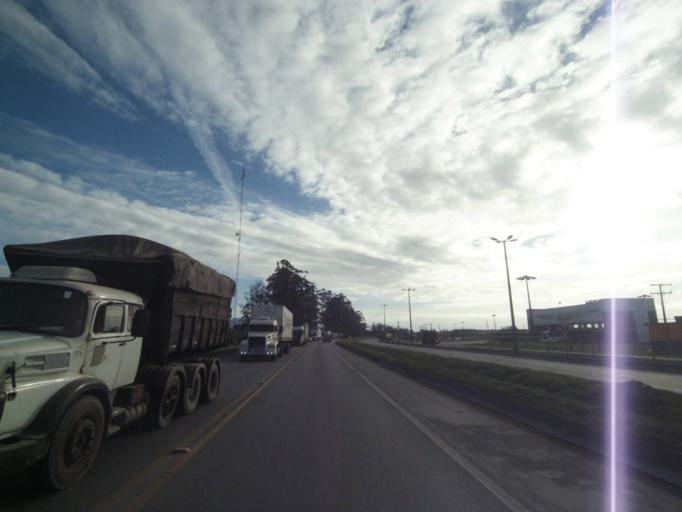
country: BR
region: Parana
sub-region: Paranagua
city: Paranagua
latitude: -25.5410
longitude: -48.5588
